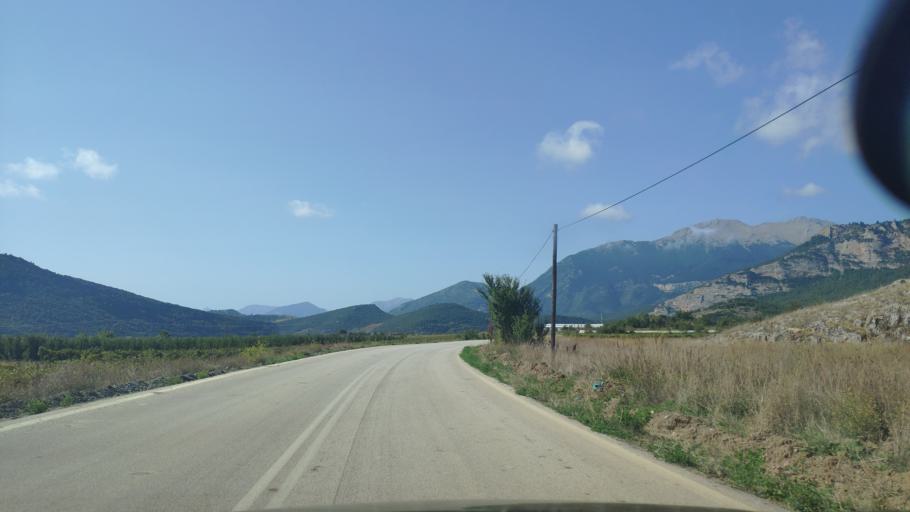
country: GR
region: Peloponnese
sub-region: Nomos Korinthias
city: Xylokastro
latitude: 37.9453
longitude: 22.5698
